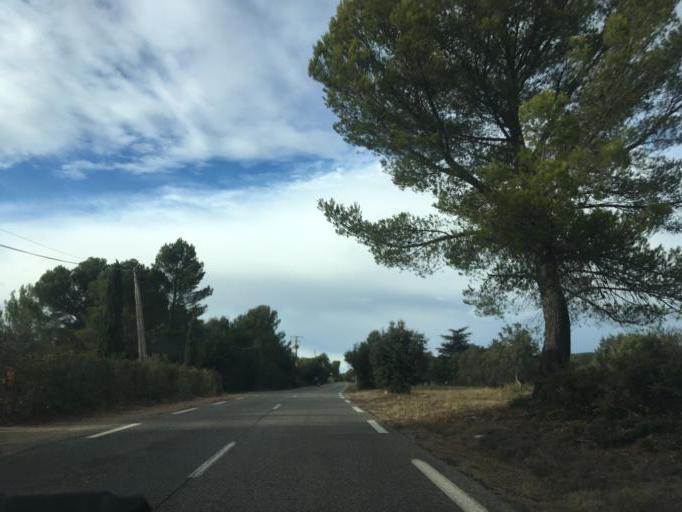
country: FR
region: Provence-Alpes-Cote d'Azur
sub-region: Departement du Var
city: Aups
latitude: 43.6149
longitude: 6.2265
